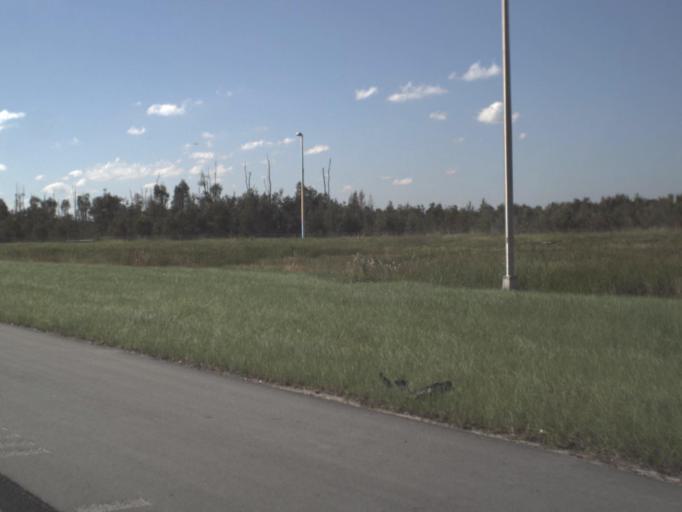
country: US
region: Florida
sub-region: Miami-Dade County
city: Doral
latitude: 25.8381
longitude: -80.3872
